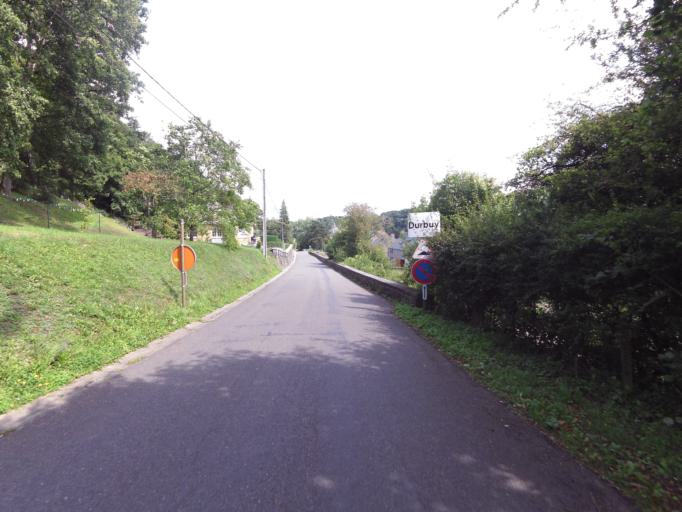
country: BE
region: Wallonia
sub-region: Province du Luxembourg
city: Durbuy
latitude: 50.3504
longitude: 5.4473
